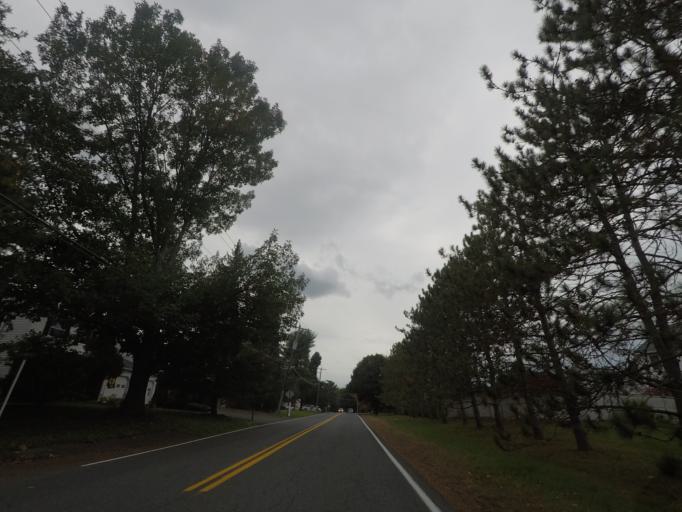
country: US
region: New York
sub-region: Albany County
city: McKownville
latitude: 42.6601
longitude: -73.8320
